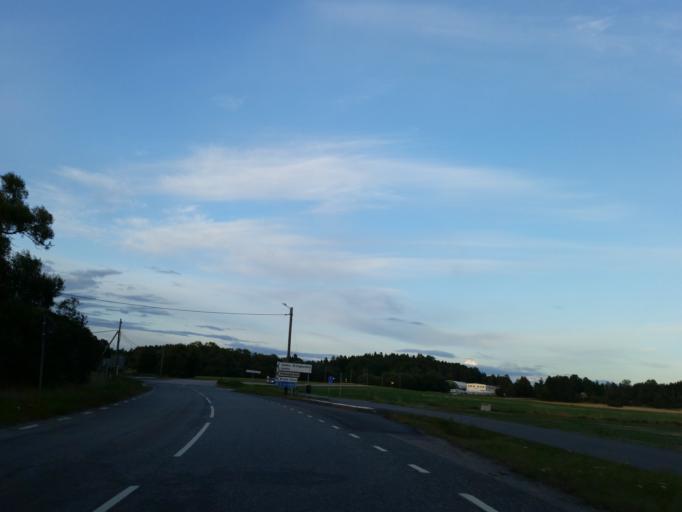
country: SE
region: Stockholm
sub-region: Sigtuna Kommun
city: Marsta
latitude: 59.6306
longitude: 17.8810
